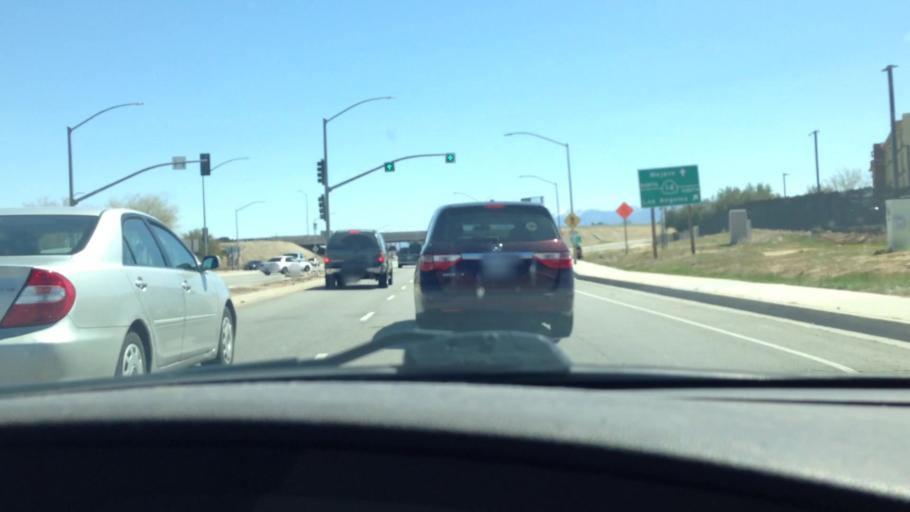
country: US
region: California
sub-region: Los Angeles County
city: Desert View Highlands
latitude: 34.5823
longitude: -118.1361
